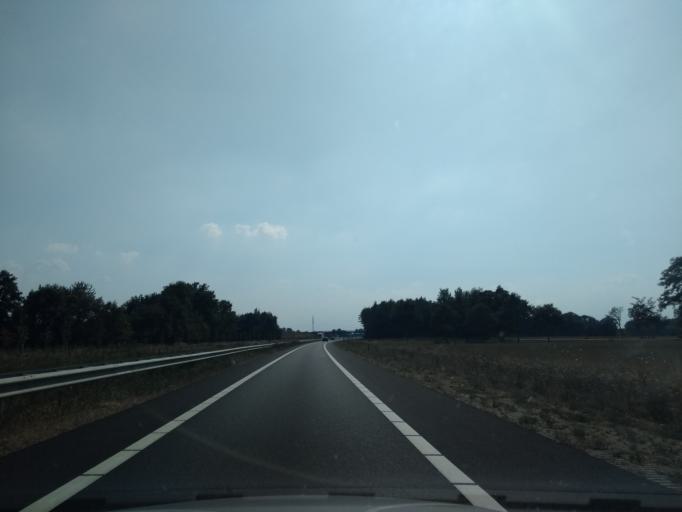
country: NL
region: Overijssel
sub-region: Gemeente Haaksbergen
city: Haaksbergen
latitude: 52.1661
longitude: 6.7065
